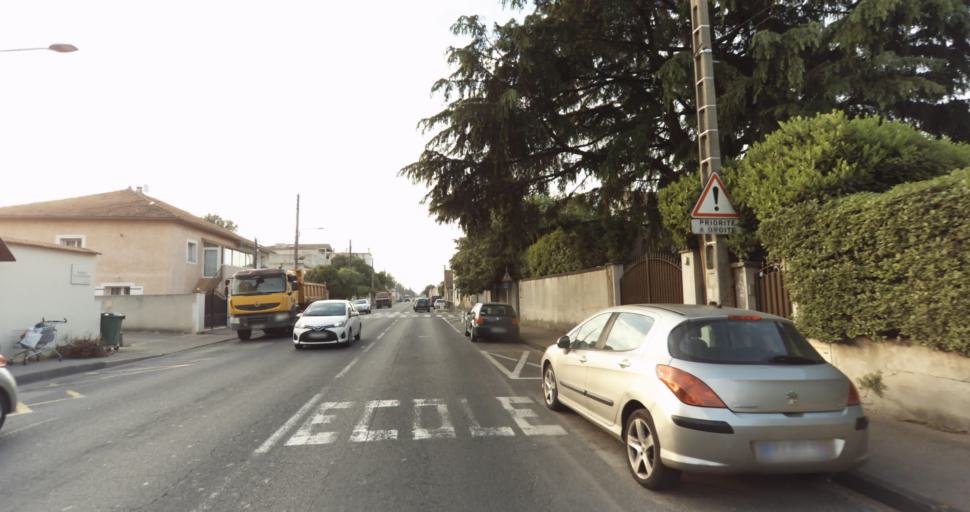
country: FR
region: Languedoc-Roussillon
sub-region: Departement du Gard
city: Nimes
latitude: 43.8267
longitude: 4.3759
